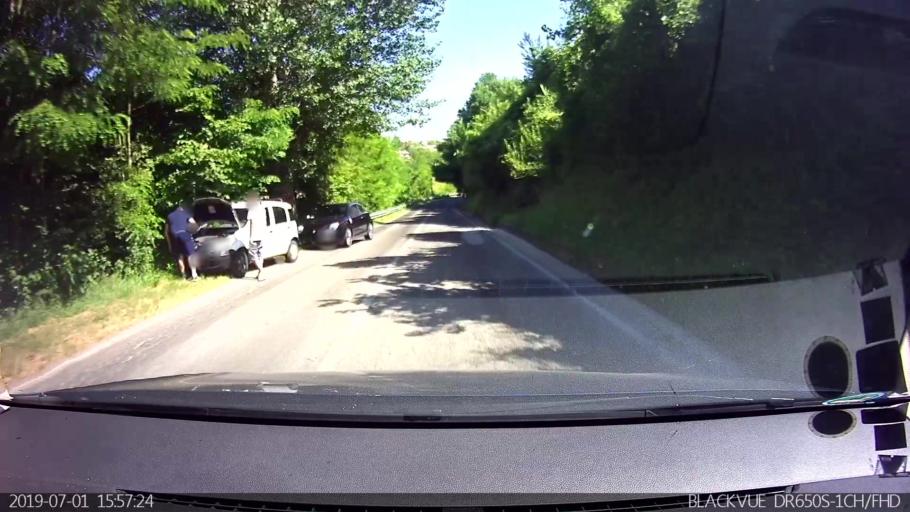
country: IT
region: Latium
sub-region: Provincia di Frosinone
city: Sant'Angelo in Villa-Giglio
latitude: 41.6766
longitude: 13.4216
